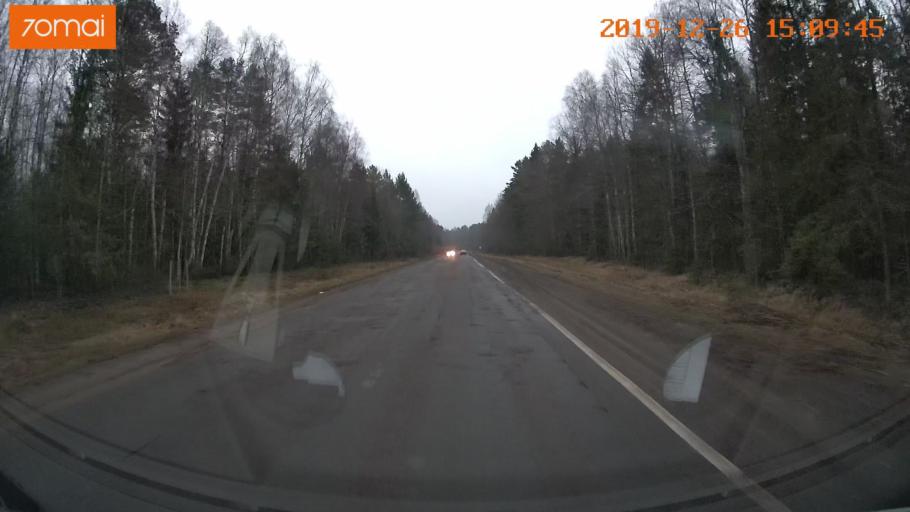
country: RU
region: Jaroslavl
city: Rybinsk
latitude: 58.1463
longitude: 38.8440
